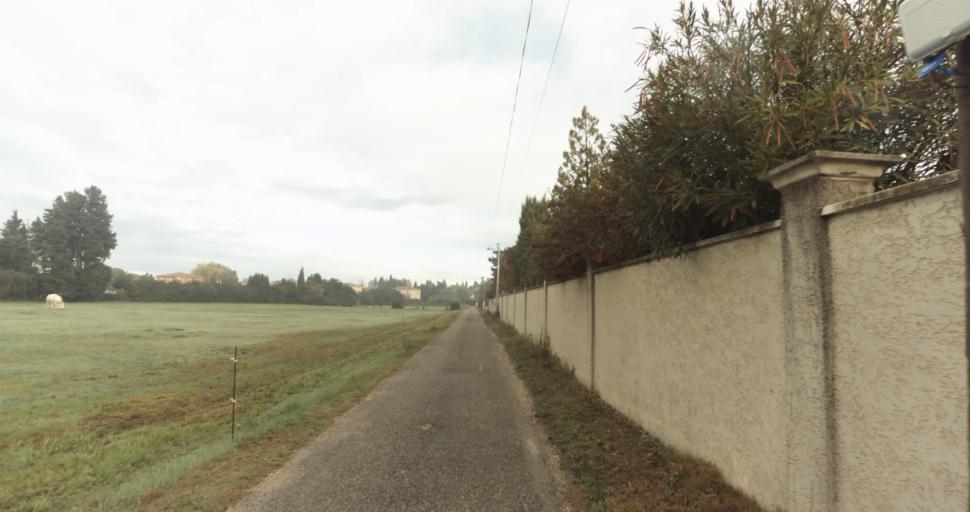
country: FR
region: Provence-Alpes-Cote d'Azur
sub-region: Departement des Bouches-du-Rhone
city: Rognonas
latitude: 43.9026
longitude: 4.8016
